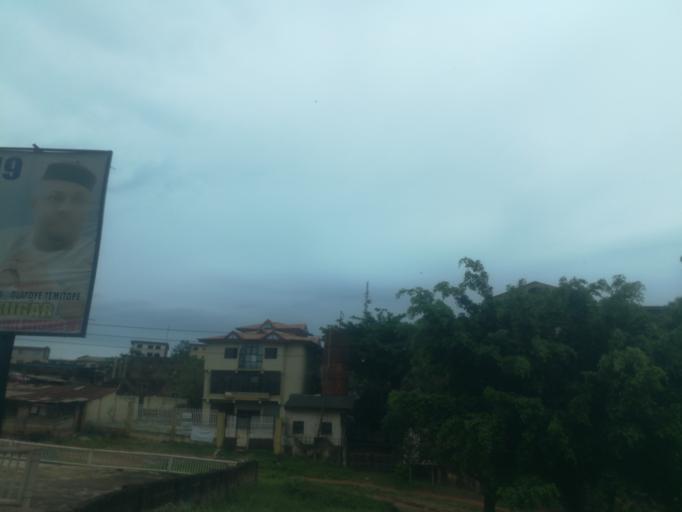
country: NG
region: Oyo
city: Ibadan
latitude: 7.3439
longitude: 3.9156
